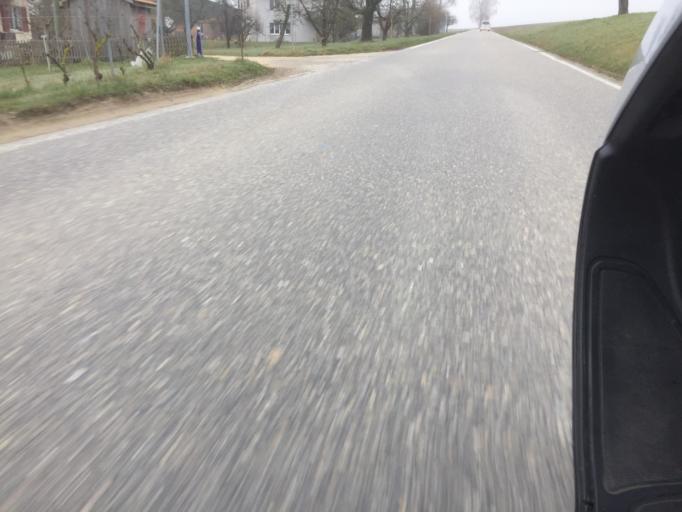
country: CH
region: Bern
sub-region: Seeland District
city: Grossaffoltern
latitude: 47.0825
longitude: 7.3888
